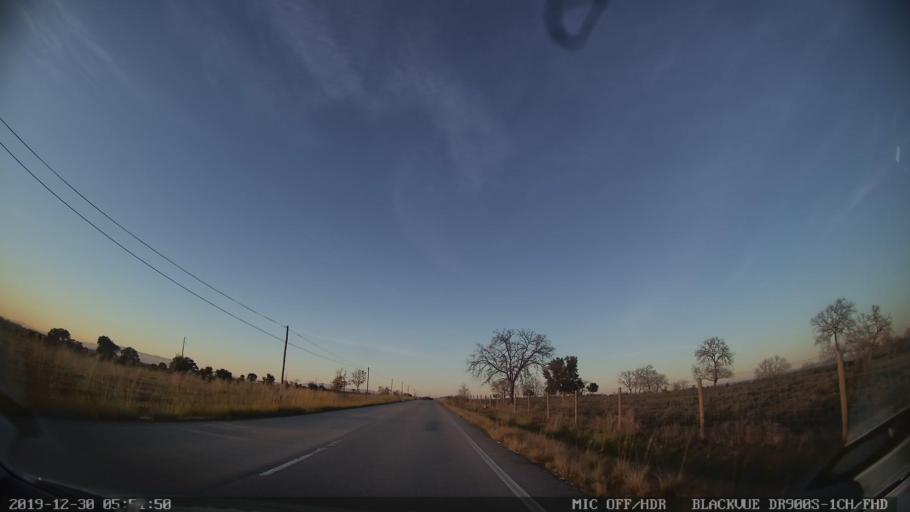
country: PT
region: Castelo Branco
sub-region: Idanha-A-Nova
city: Idanha-a-Nova
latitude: 39.9994
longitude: -7.2465
